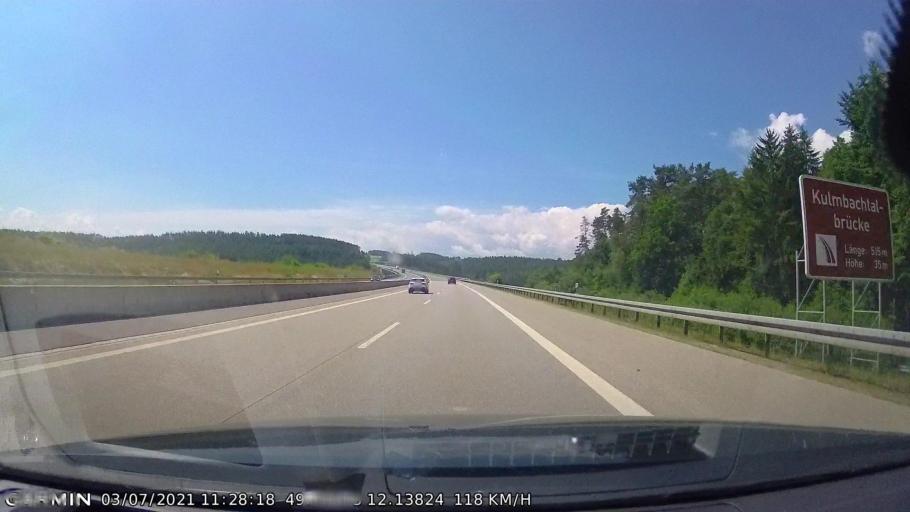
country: DE
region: Bavaria
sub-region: Upper Palatinate
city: Pfreimd
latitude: 49.4865
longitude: 12.1382
